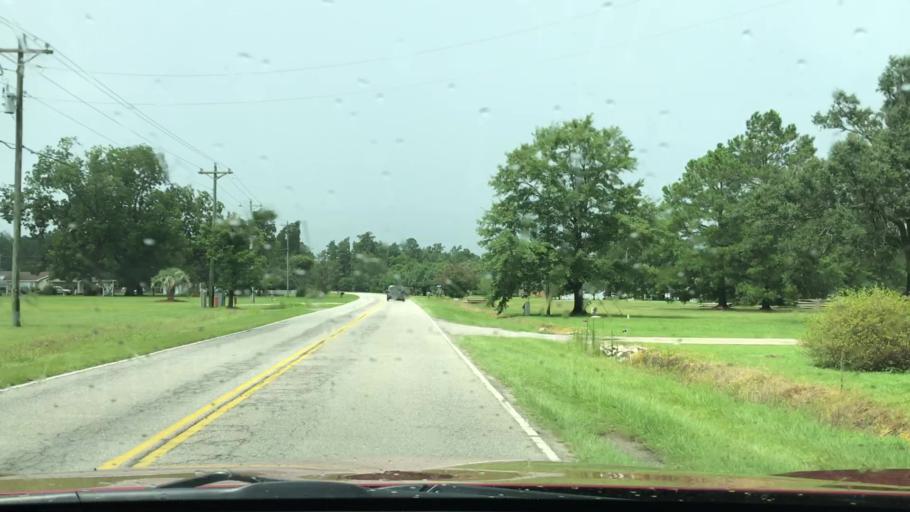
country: US
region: South Carolina
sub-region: Horry County
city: Red Hill
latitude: 33.8876
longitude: -78.9577
